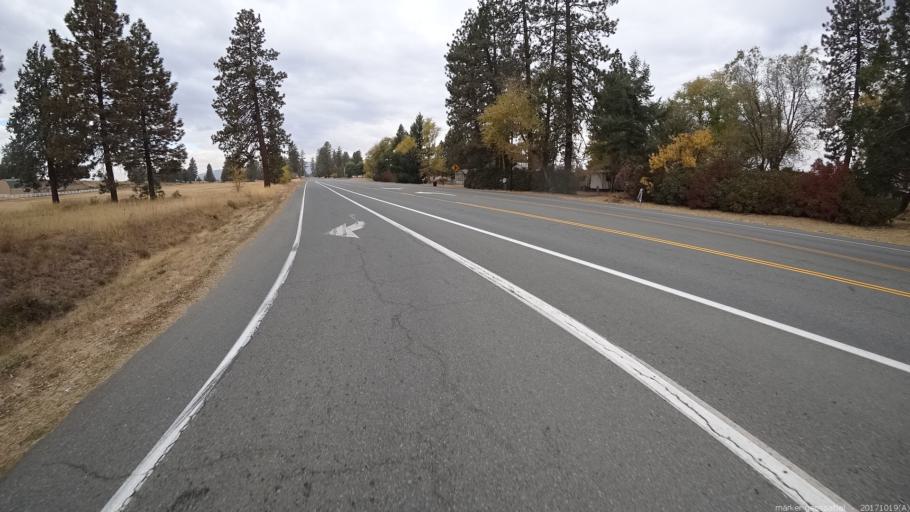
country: US
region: California
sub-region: Shasta County
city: Burney
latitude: 41.0588
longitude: -121.3756
